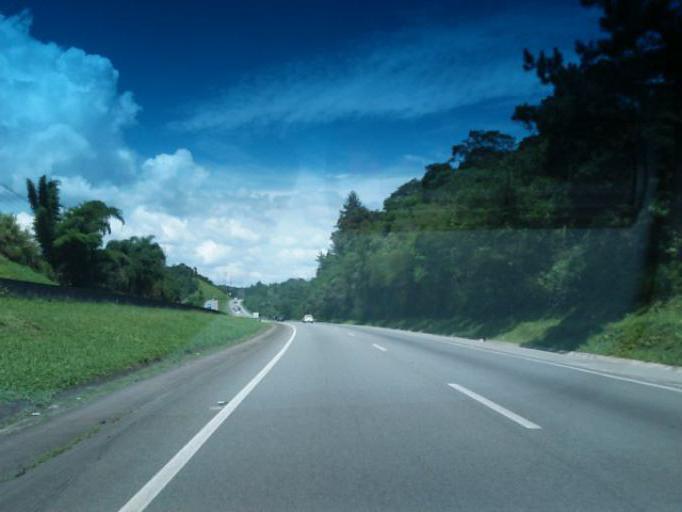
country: BR
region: Sao Paulo
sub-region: Juquitiba
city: Juquitiba
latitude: -23.9401
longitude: -47.0457
